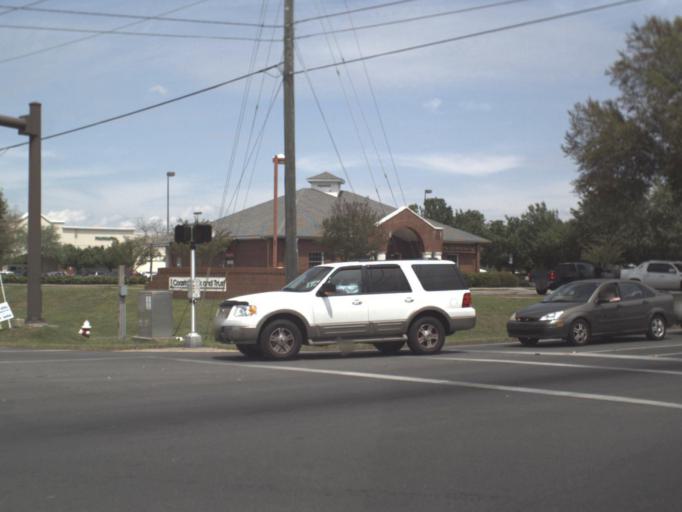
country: US
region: Florida
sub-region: Escambia County
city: Ensley
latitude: 30.5342
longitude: -87.3132
